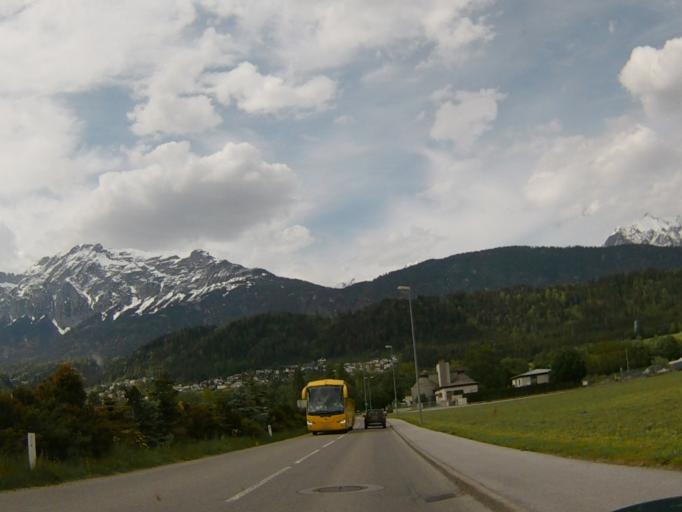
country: AT
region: Tyrol
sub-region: Politischer Bezirk Innsbruck Land
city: Wattenberg
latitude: 47.2963
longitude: 11.6048
